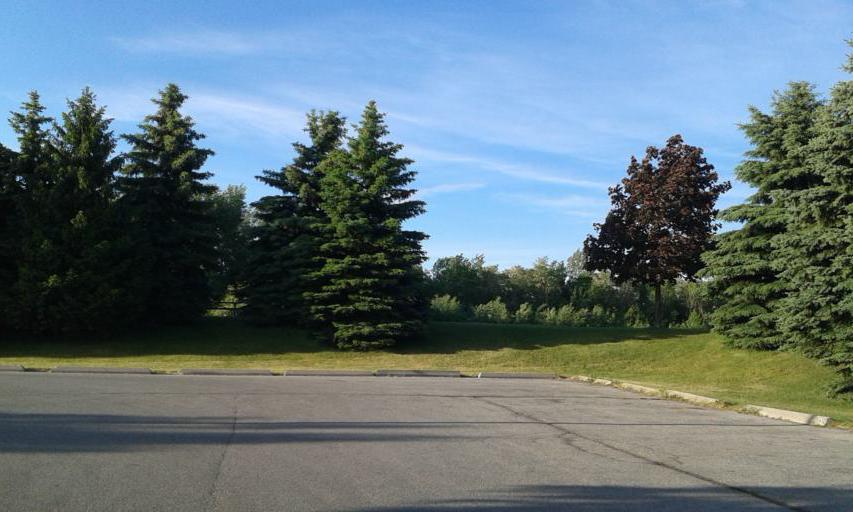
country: CA
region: Ontario
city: Markham
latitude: 43.8305
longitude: -79.2703
